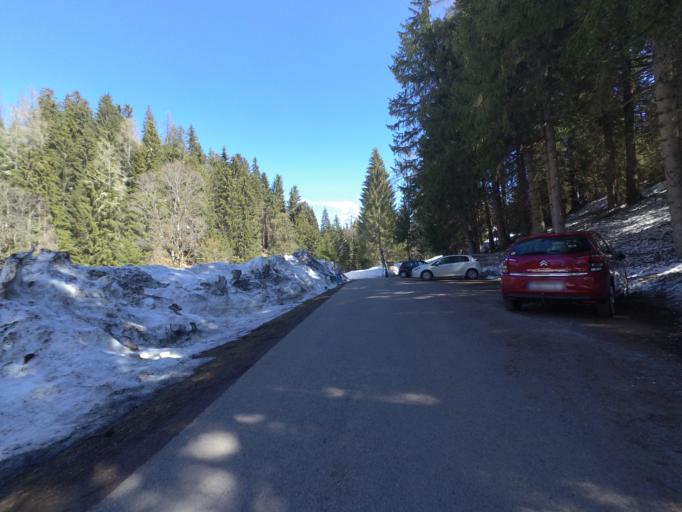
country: AT
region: Salzburg
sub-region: Politischer Bezirk Sankt Johann im Pongau
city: Sankt Veit im Pongau
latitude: 47.3408
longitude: 13.1608
